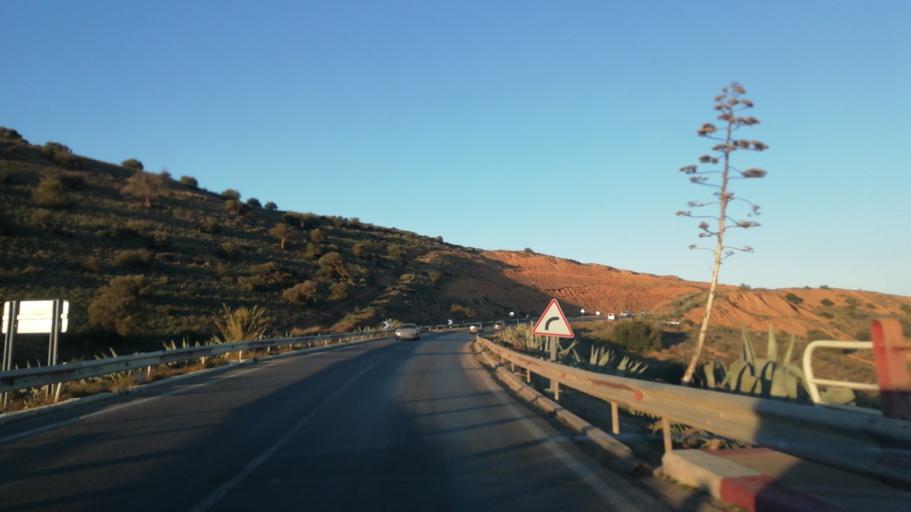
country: DZ
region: Tlemcen
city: Nedroma
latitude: 34.8896
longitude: -1.6688
